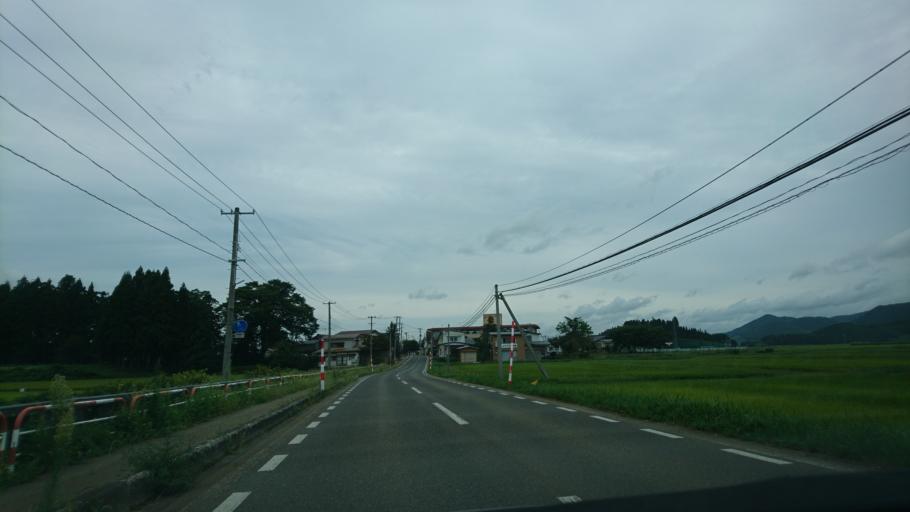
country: JP
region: Akita
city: Yuzawa
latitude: 39.1737
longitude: 140.5564
